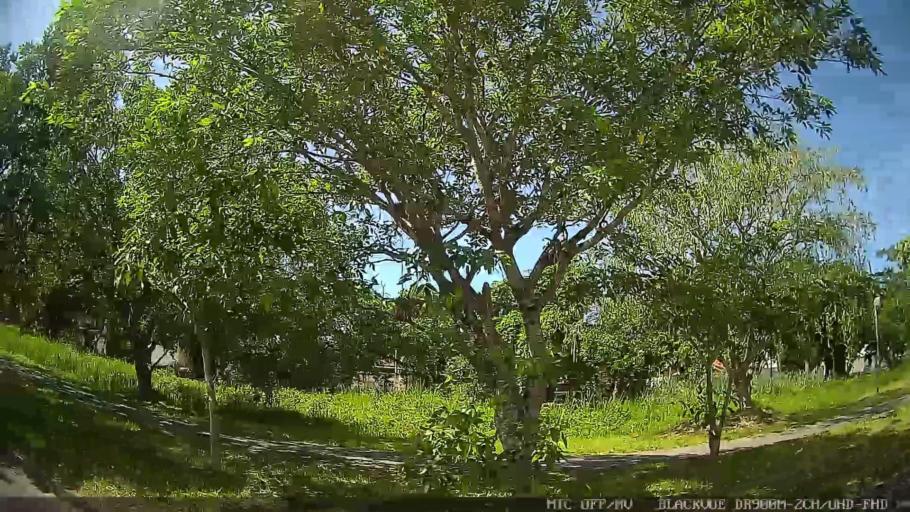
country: BR
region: Sao Paulo
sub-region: Peruibe
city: Peruibe
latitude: -24.3149
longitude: -47.0028
